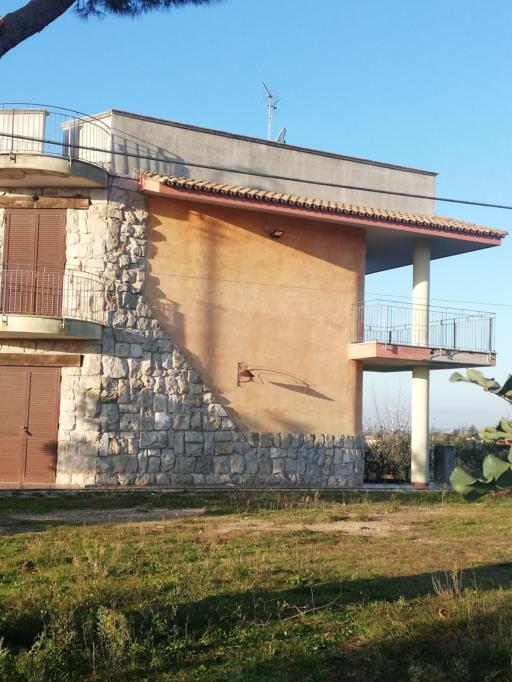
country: IT
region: Apulia
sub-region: Provincia di Bari
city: Gravina in Puglia
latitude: 40.8531
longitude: 16.3433
